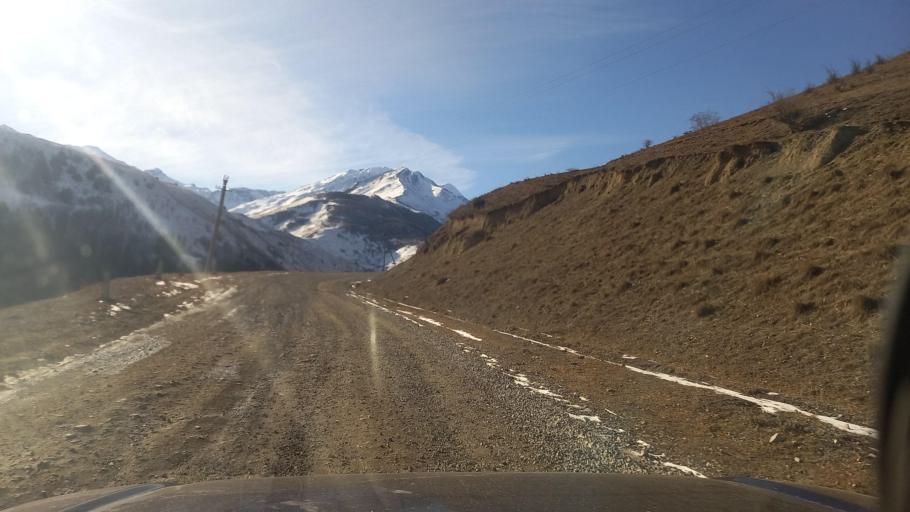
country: RU
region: Ingushetiya
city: Dzhayrakh
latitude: 42.8408
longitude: 44.4993
